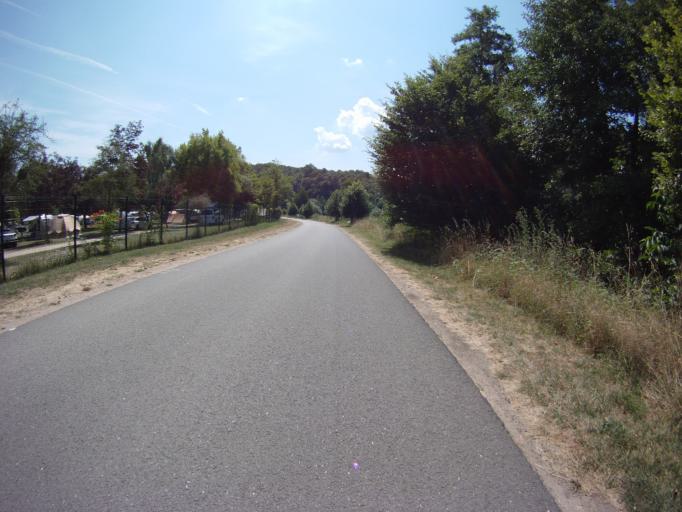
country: FR
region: Lorraine
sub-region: Departement de Meurthe-et-Moselle
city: Liverdun
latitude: 48.7483
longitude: 6.0562
